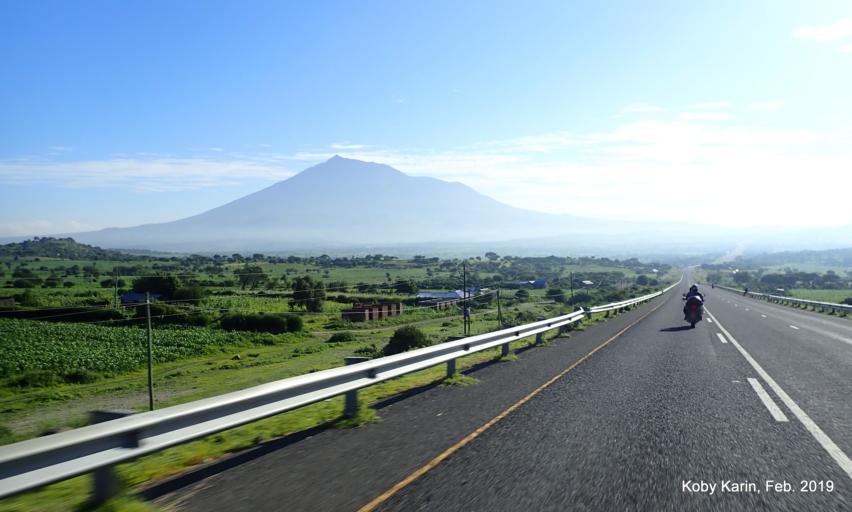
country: TZ
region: Manyara
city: Katesh
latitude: -4.5229
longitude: 35.2932
